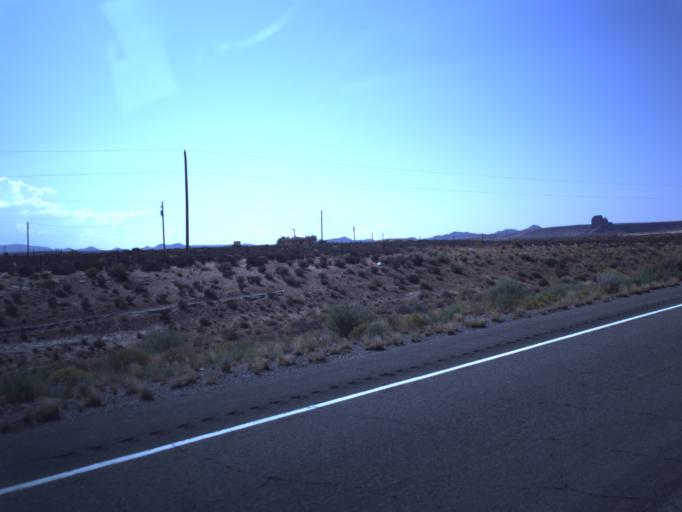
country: US
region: Utah
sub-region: San Juan County
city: Blanding
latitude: 37.0725
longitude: -109.5504
